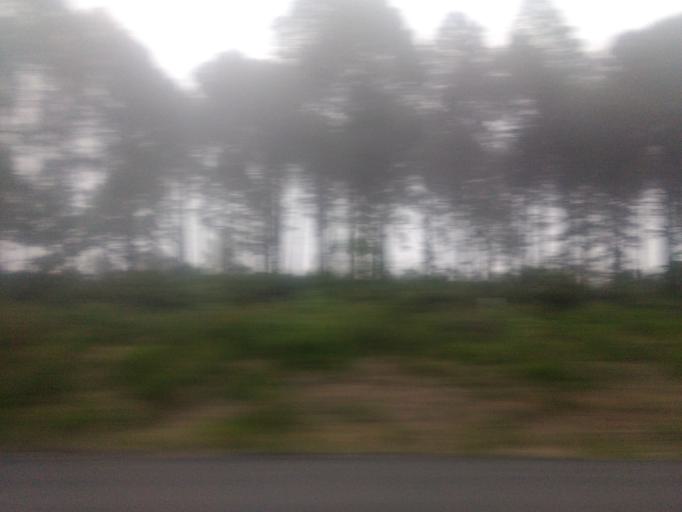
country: MX
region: Veracruz
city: Las Vigas
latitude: 19.6303
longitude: -97.1100
